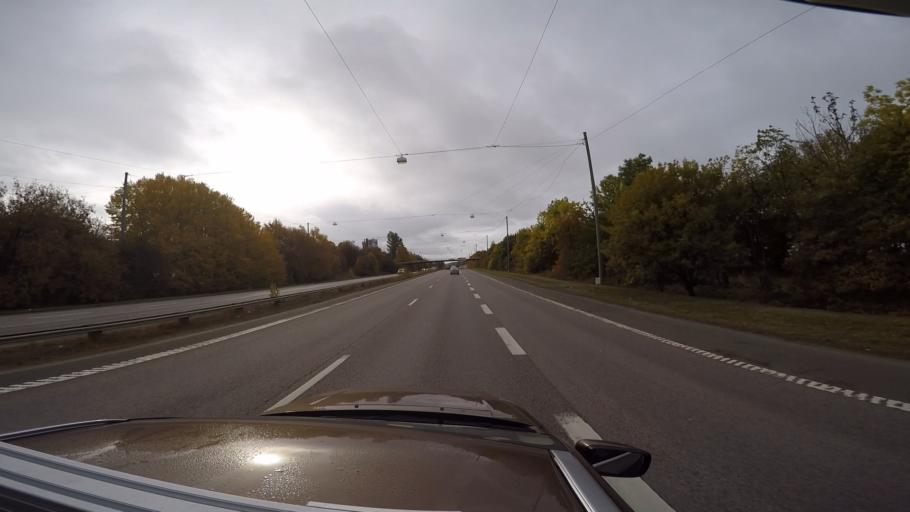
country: SE
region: Vaestra Goetaland
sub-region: Goteborg
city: Majorna
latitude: 57.6656
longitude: 11.9369
